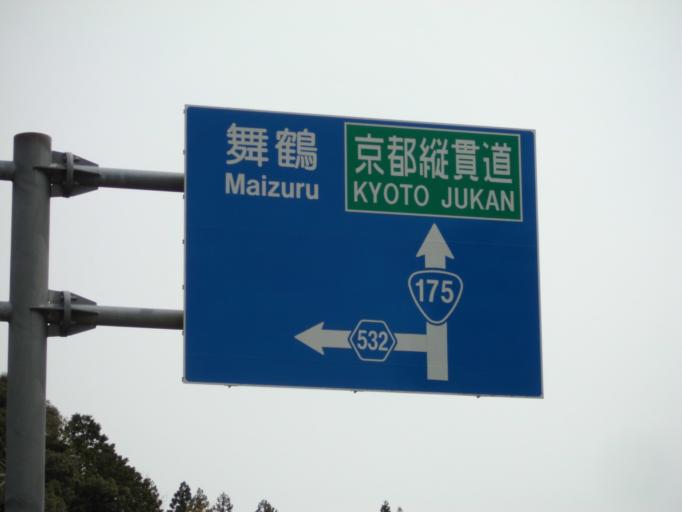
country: JP
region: Kyoto
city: Miyazu
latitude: 35.4104
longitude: 135.1901
